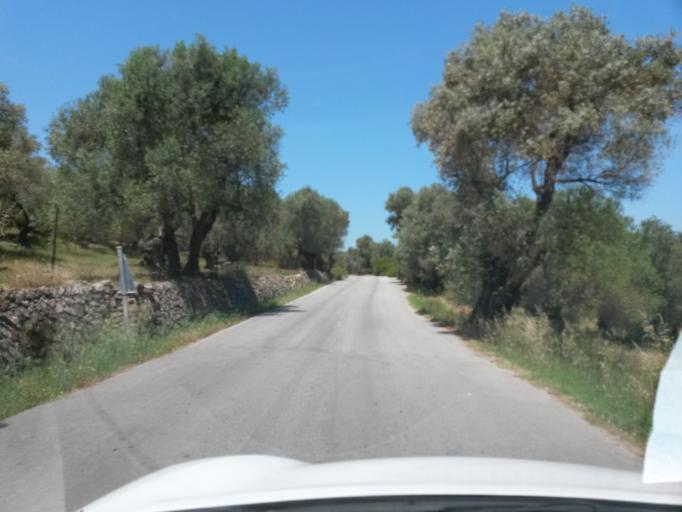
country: GR
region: North Aegean
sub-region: Nomos Lesvou
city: Pamfylla
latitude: 39.2099
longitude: 26.4726
